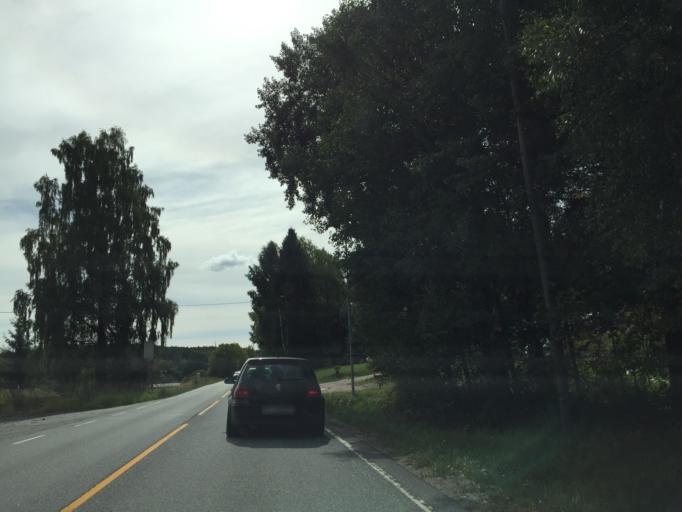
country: NO
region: Ostfold
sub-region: Fredrikstad
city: Fredrikstad
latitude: 59.2716
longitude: 10.8985
